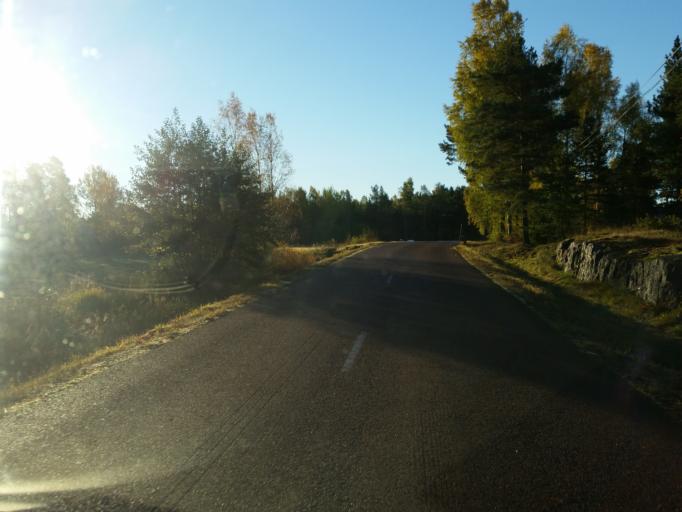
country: AX
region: Alands skaergard
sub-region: Vardoe
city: Vardoe
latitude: 60.2959
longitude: 20.3853
